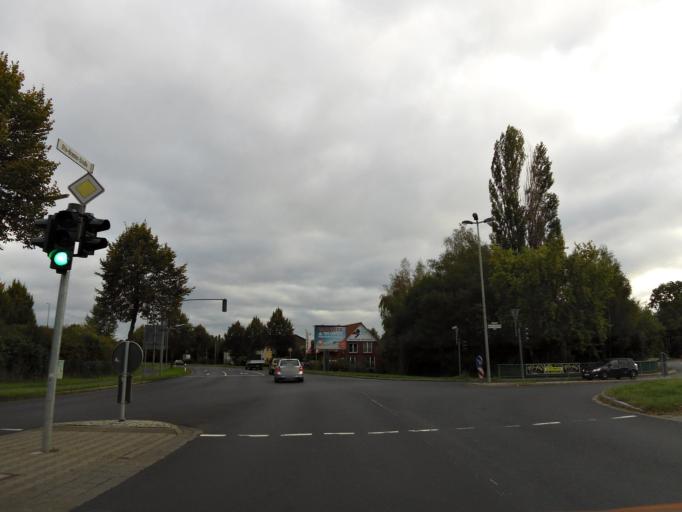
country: DE
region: Lower Saxony
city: Goettingen
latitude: 51.5433
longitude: 9.8885
